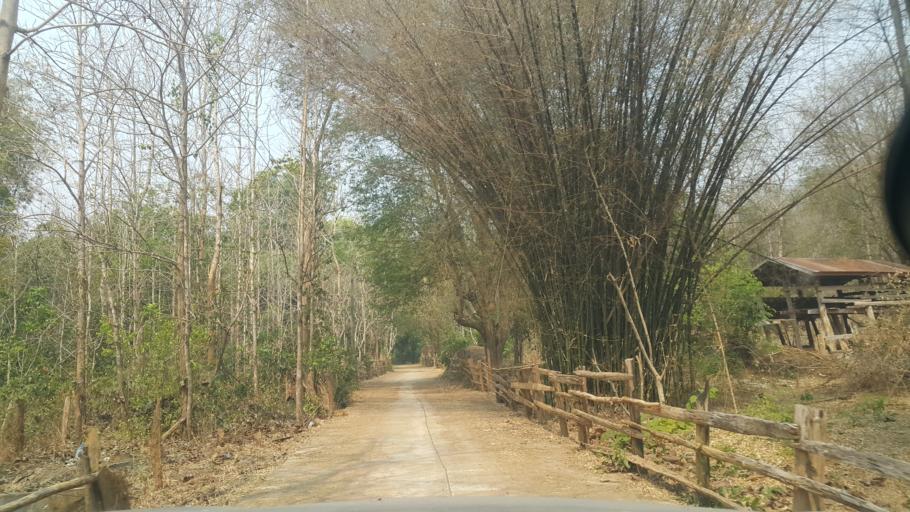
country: TH
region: Lampang
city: Sop Prap
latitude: 17.8068
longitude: 99.2559
